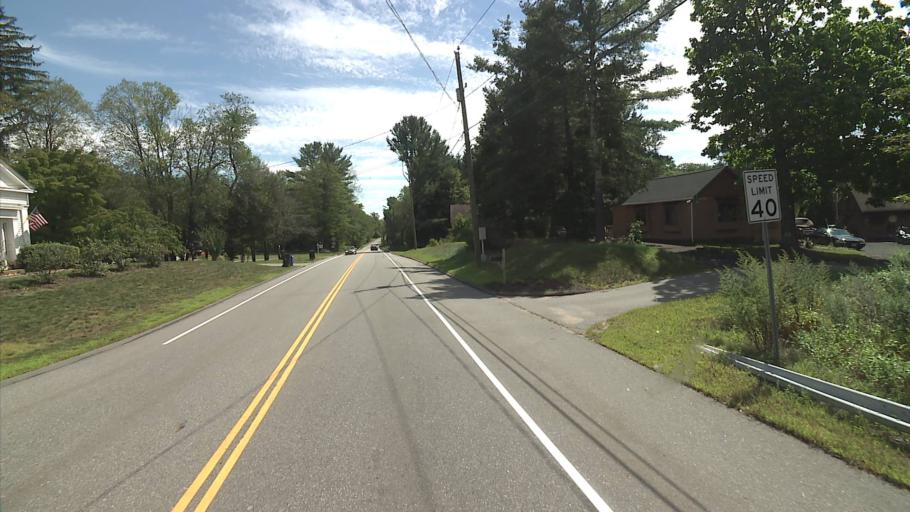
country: US
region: Connecticut
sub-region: Tolland County
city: Mansfield City
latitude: 41.7704
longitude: -72.2029
